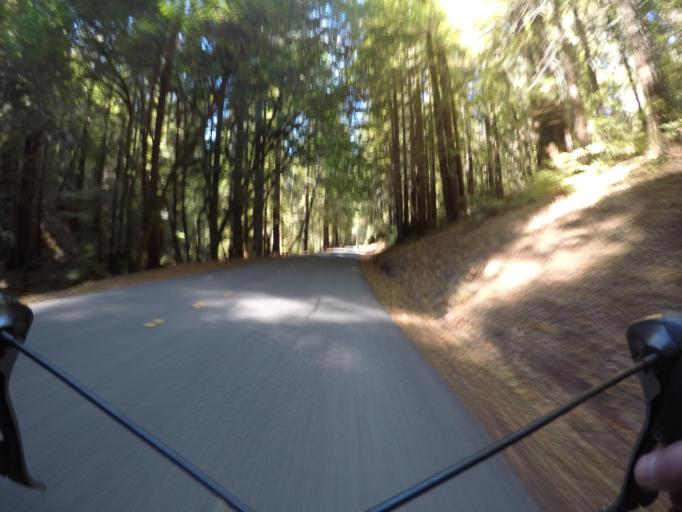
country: US
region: California
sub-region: San Mateo County
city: Portola Valley
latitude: 37.2977
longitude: -122.2521
